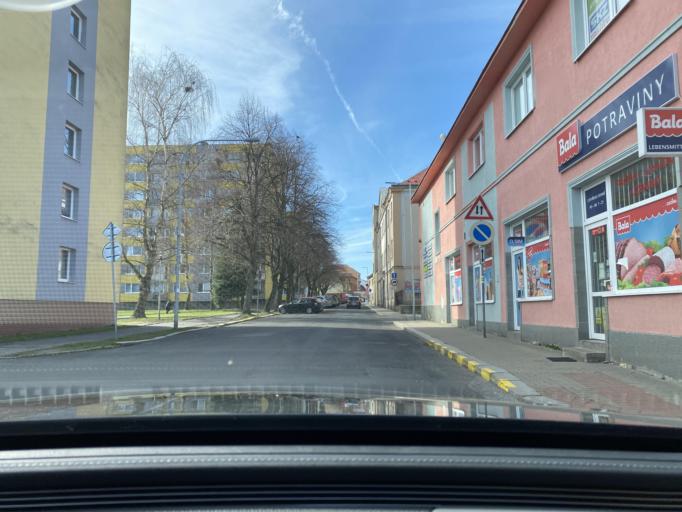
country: CZ
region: Ustecky
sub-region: Okres Decin
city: Rumburk
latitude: 50.9503
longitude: 14.5618
